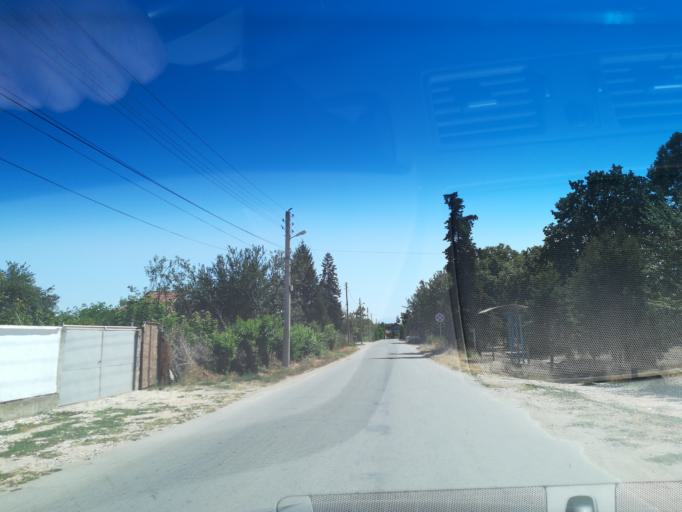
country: BG
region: Pazardzhik
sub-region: Obshtina Pazardzhik
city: Pazardzhik
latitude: 42.2708
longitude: 24.4021
